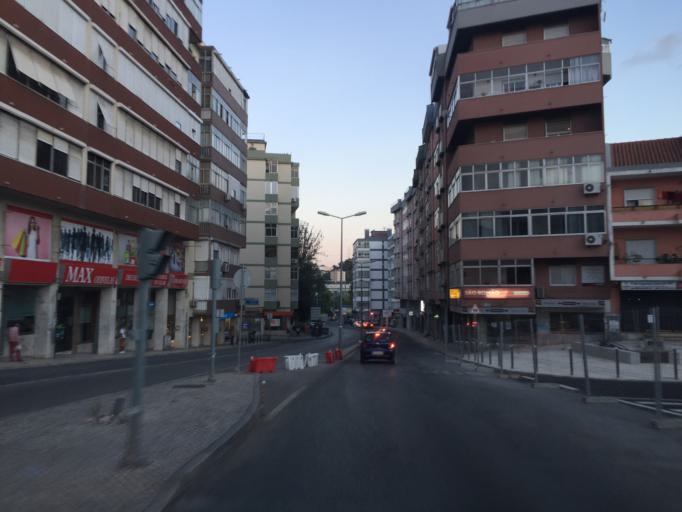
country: PT
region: Lisbon
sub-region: Odivelas
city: Odivelas
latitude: 38.7905
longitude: -9.1761
